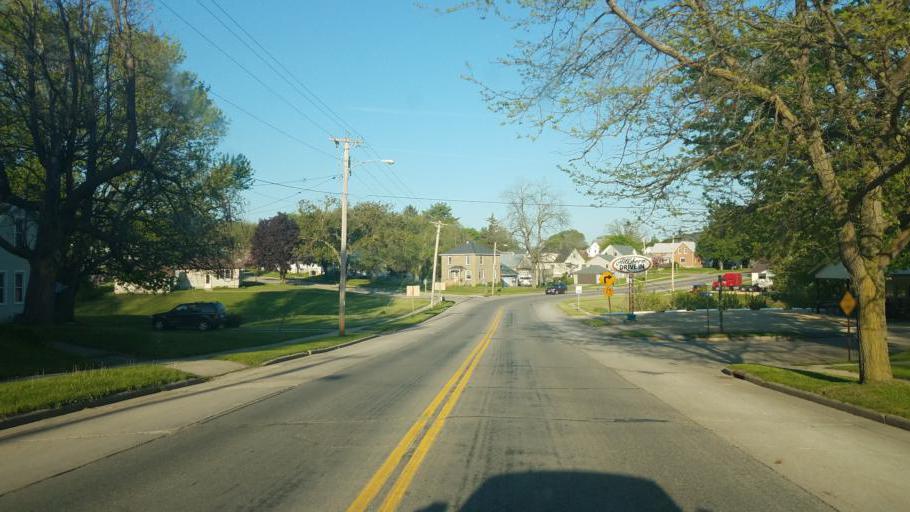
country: US
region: Wisconsin
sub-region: Vernon County
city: Hillsboro
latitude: 43.6522
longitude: -90.3479
